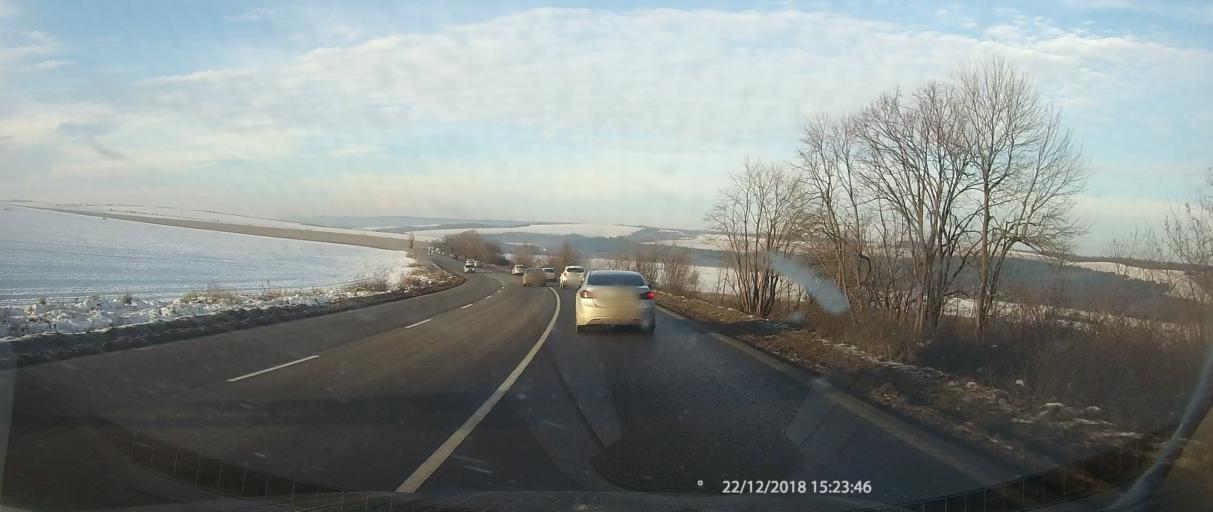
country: BG
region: Ruse
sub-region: Obshtina Ivanovo
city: Ivanovo
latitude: 43.7274
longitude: 25.9193
